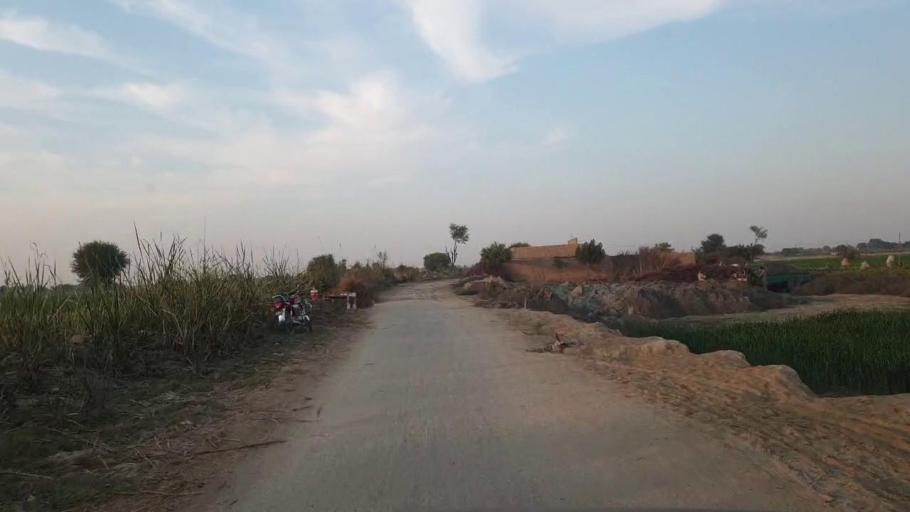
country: PK
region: Sindh
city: Shahpur Chakar
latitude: 26.1916
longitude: 68.6173
